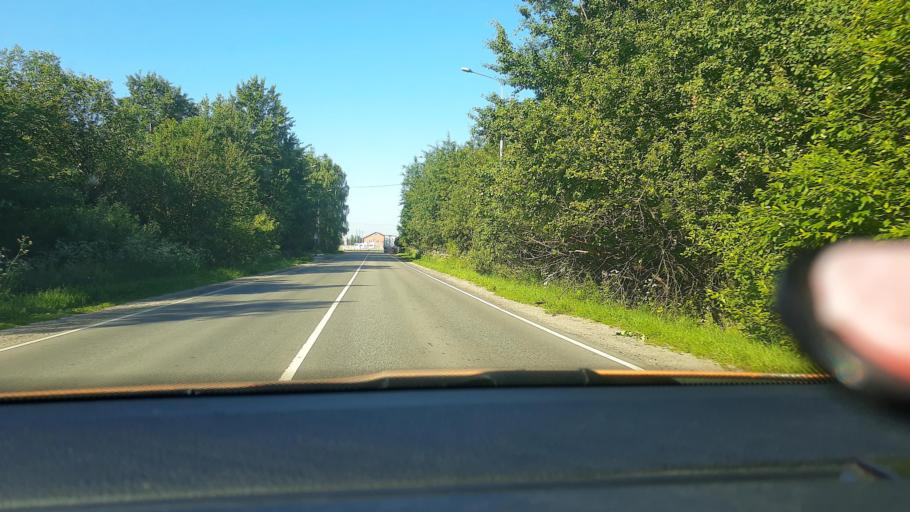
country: RU
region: Moskovskaya
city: Pavlovskiy Posad
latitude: 55.8574
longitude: 38.6696
